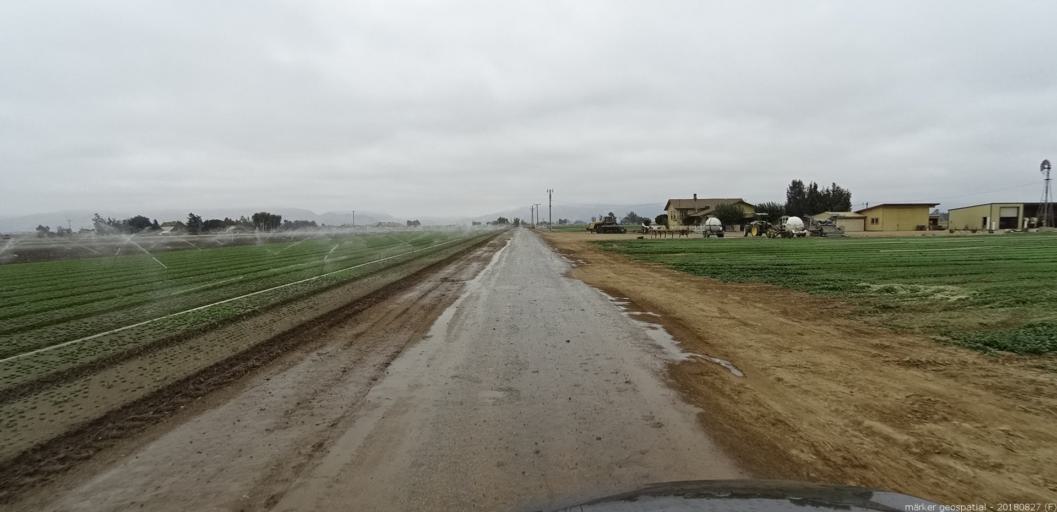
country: US
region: California
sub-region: Monterey County
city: Greenfield
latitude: 36.3393
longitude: -121.2418
